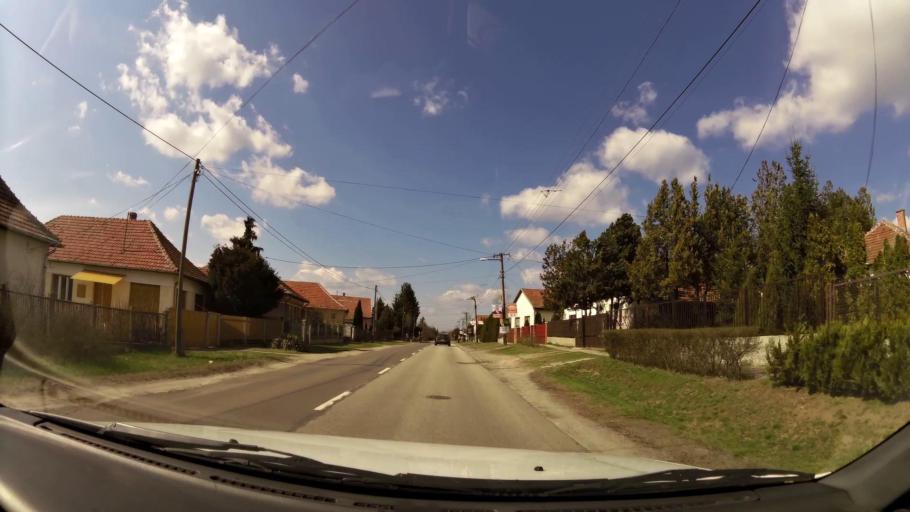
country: HU
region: Pest
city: Farmos
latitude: 47.3544
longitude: 19.8549
